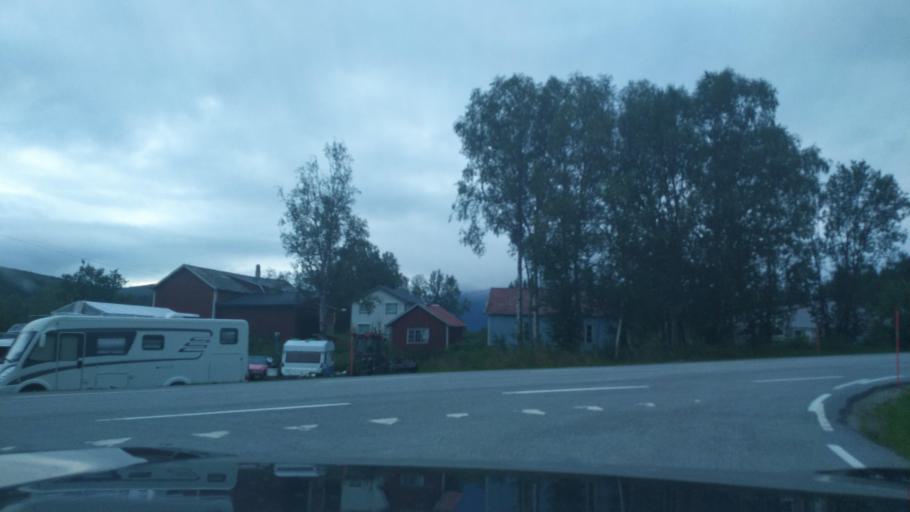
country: NO
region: Troms
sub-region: Lavangen
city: Tennevoll
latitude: 68.7492
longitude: 17.8160
